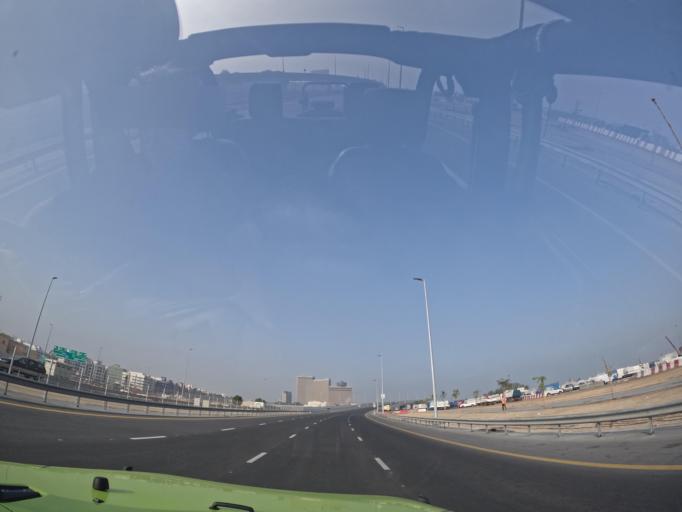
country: AE
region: Ash Shariqah
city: Sharjah
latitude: 25.2821
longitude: 55.3126
